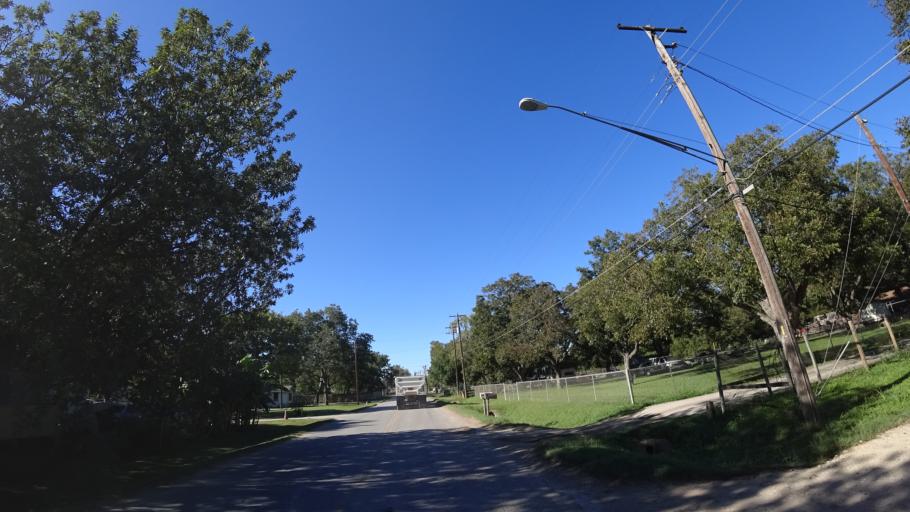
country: US
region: Texas
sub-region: Travis County
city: Austin
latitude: 30.2397
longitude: -97.6827
